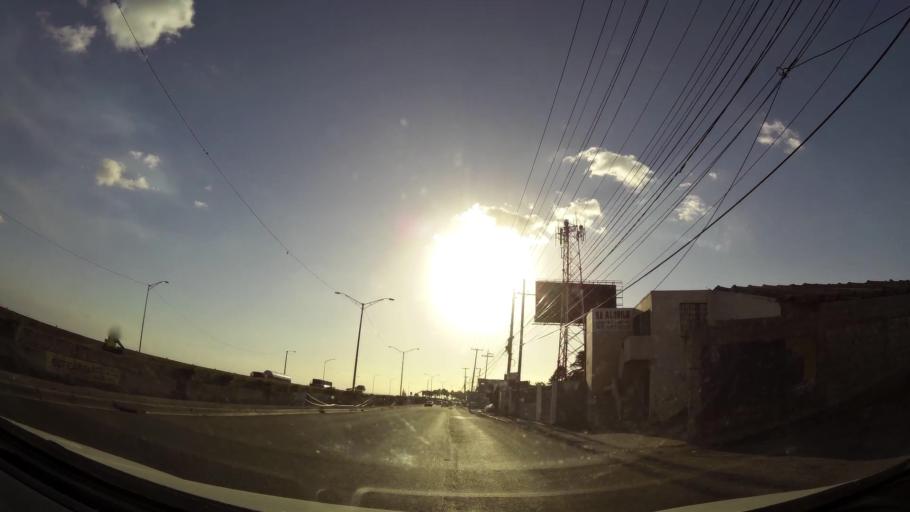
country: DO
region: Santo Domingo
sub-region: Santo Domingo
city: Santo Domingo Este
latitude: 18.4655
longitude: -69.7996
